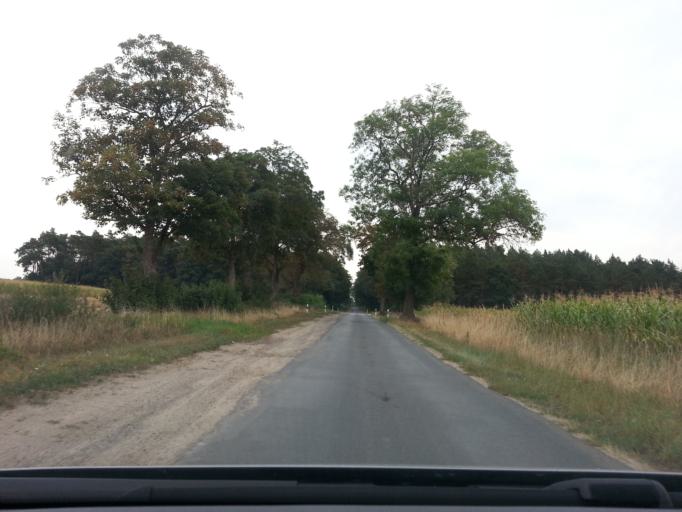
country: DE
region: Mecklenburg-Vorpommern
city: Ferdinandshof
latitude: 53.6616
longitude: 13.9044
